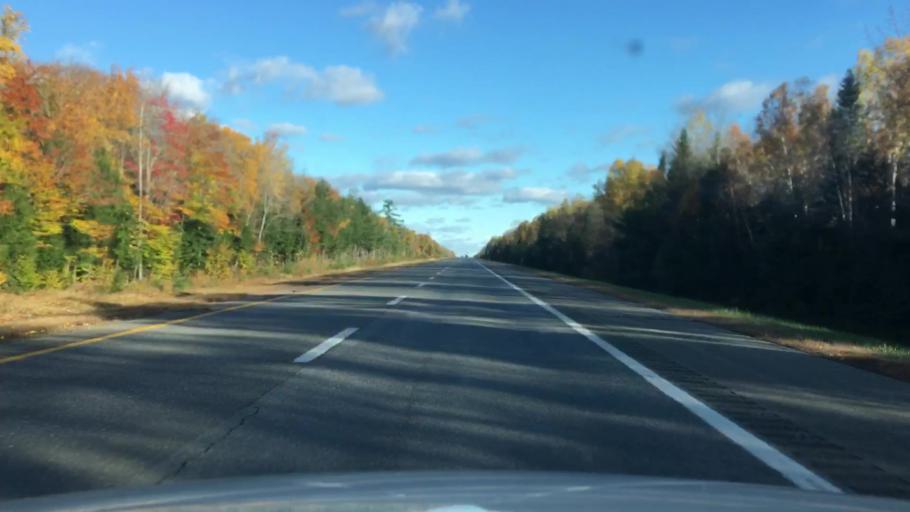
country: US
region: Maine
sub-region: Penobscot County
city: Greenbush
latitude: 45.0709
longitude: -68.6904
